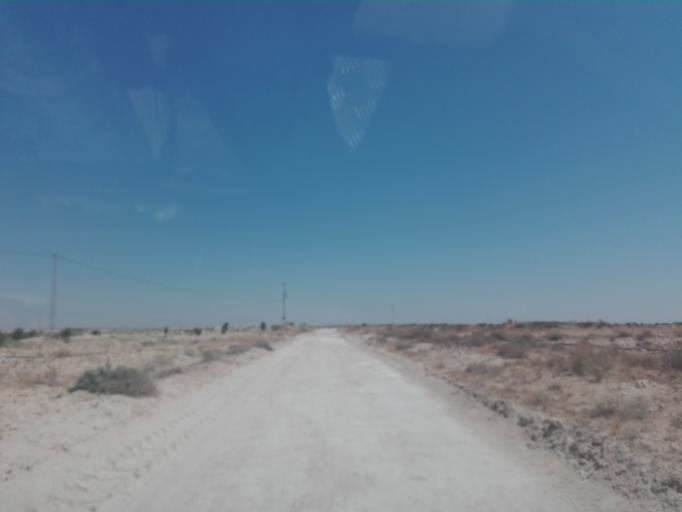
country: TN
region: Safaqis
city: Skhira
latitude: 34.3954
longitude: 9.9275
